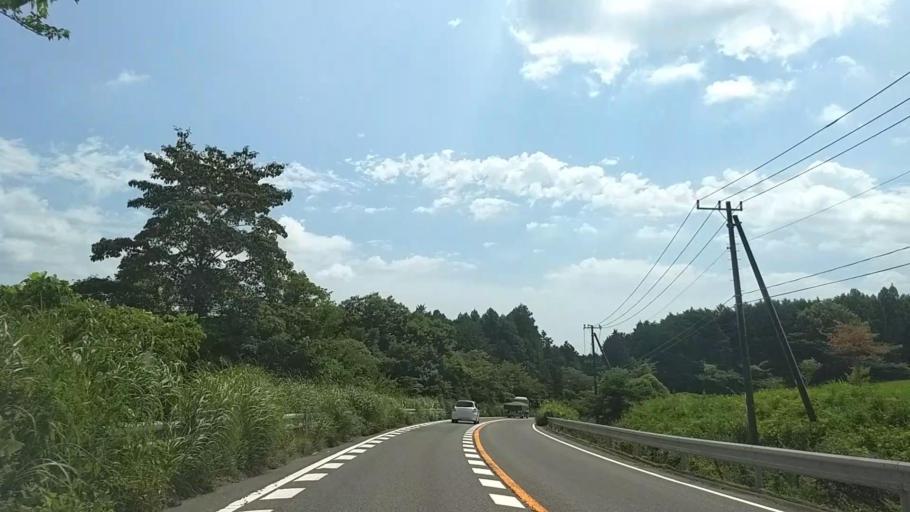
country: JP
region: Shizuoka
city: Fujinomiya
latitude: 35.3421
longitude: 138.5882
